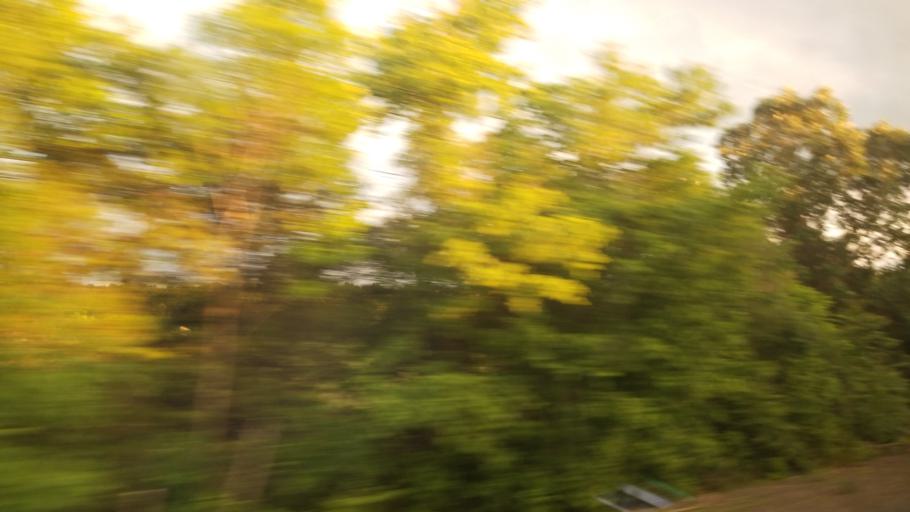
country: US
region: Virginia
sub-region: Fauquier County
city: Bealeton
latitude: 38.5246
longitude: -77.8203
